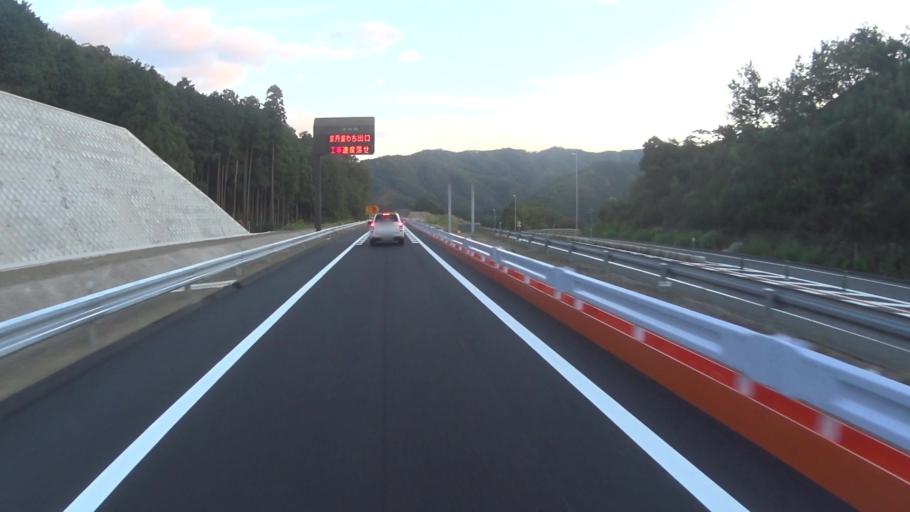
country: JP
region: Kyoto
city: Ayabe
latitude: 35.2838
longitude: 135.3372
